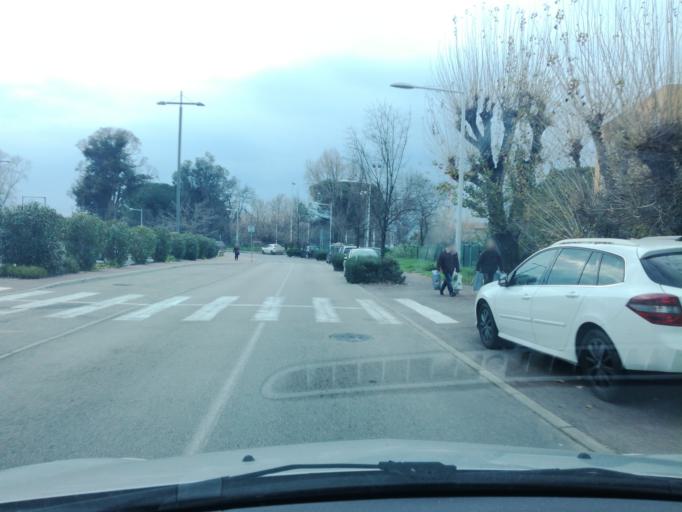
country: FR
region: Provence-Alpes-Cote d'Azur
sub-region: Departement des Alpes-Maritimes
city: Mandelieu-la-Napoule
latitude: 43.5554
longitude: 6.9632
